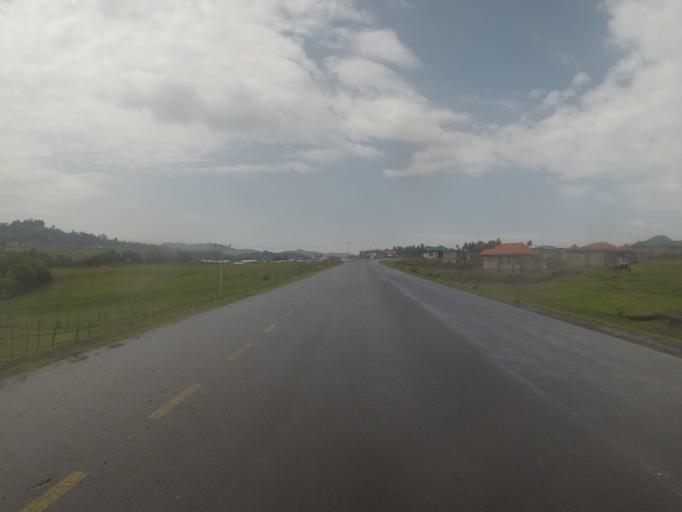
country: ET
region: Amhara
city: Debark'
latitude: 13.1333
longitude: 37.8916
